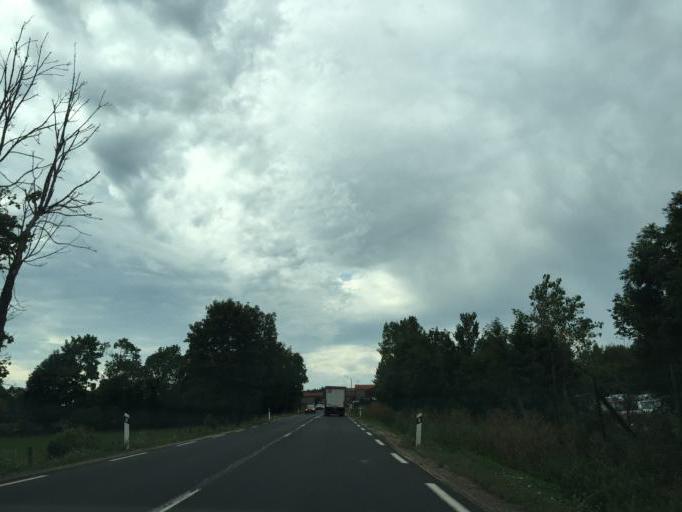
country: FR
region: Auvergne
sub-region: Departement de la Haute-Loire
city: Solignac-sur-Loire
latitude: 44.9487
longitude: 3.8464
